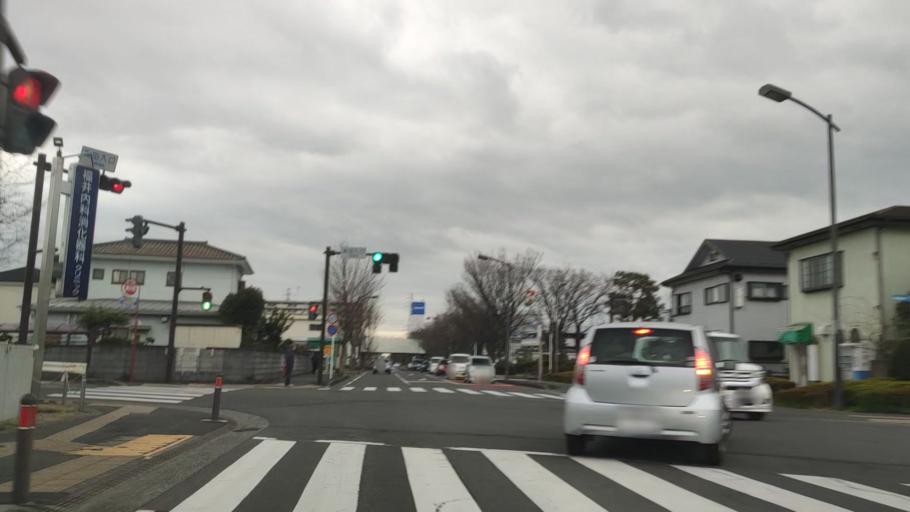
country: JP
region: Kanagawa
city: Odawara
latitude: 35.2855
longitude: 139.1893
